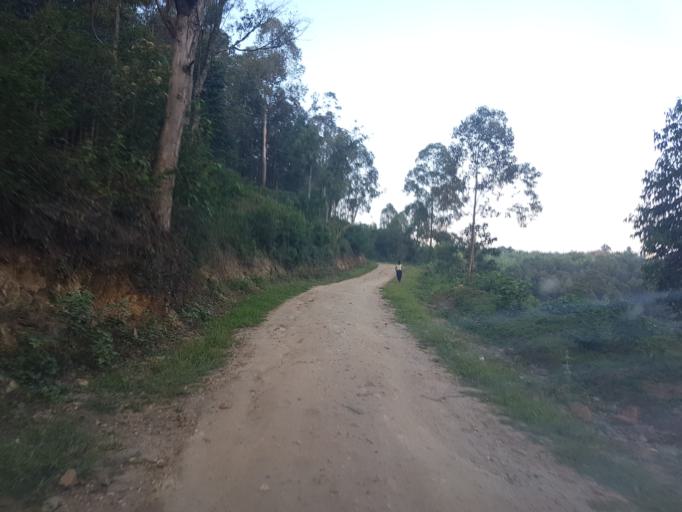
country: UG
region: Western Region
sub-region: Mitoma District
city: Mitoma
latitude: -0.6799
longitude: 29.9156
